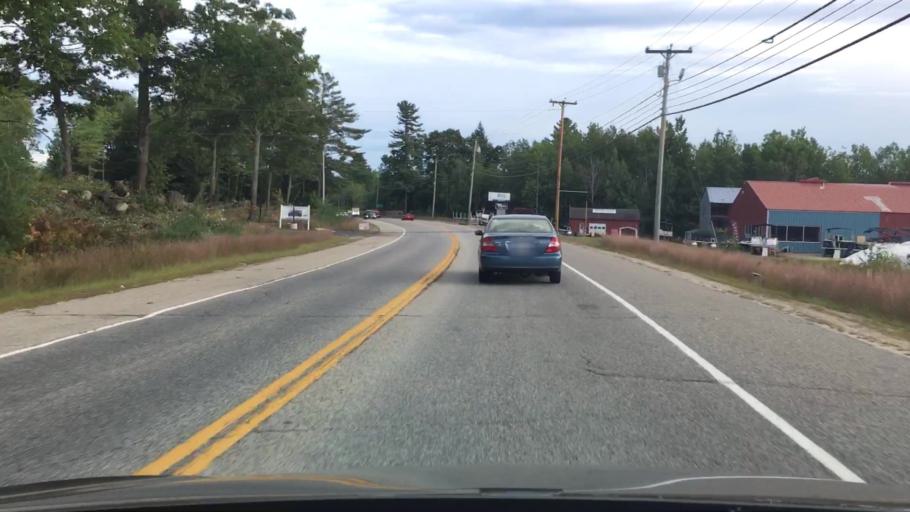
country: US
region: Maine
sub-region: Cumberland County
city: Bridgton
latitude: 44.0363
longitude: -70.6997
